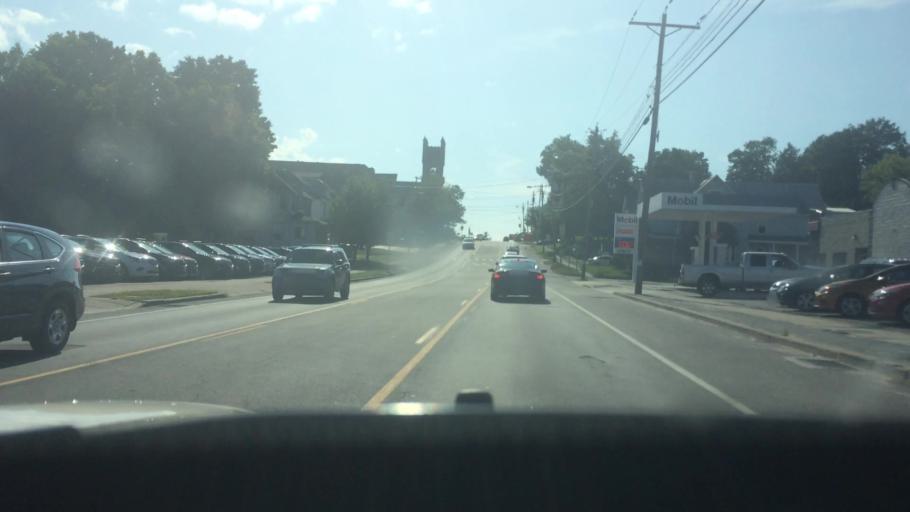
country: US
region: New York
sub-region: Franklin County
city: Malone
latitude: 44.8497
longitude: -74.2841
